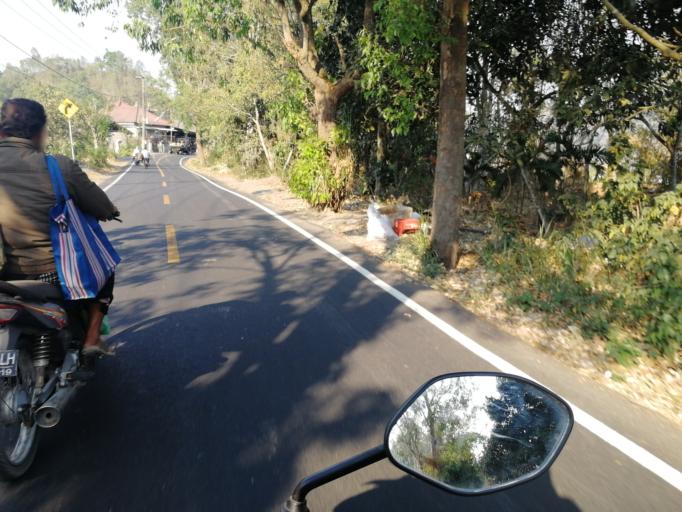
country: ID
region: Bali
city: Banjar Trunyan
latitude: -8.2421
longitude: 115.4029
